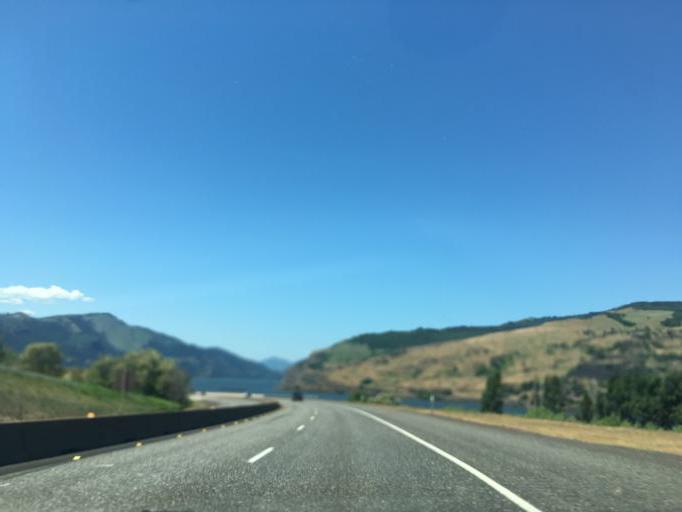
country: US
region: Washington
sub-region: Klickitat County
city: White Salmon
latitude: 45.6955
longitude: -121.3744
